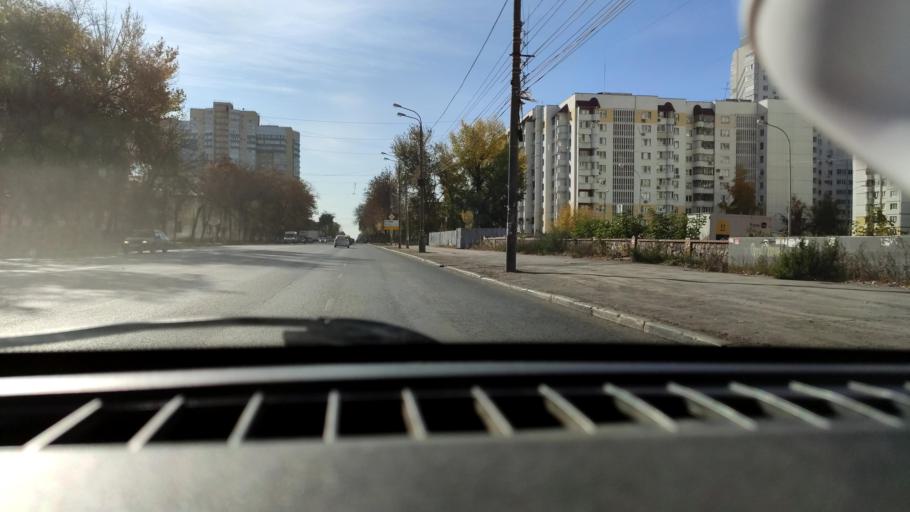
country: RU
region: Samara
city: Samara
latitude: 53.2086
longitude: 50.1895
